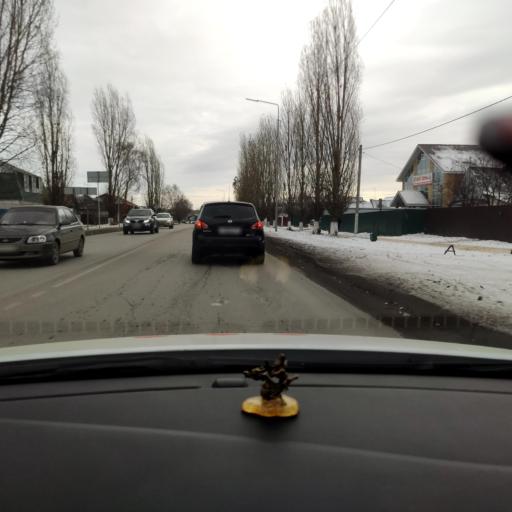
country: RU
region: Tatarstan
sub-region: Zelenodol'skiy Rayon
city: Zelenodolsk
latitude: 55.8477
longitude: 48.5307
